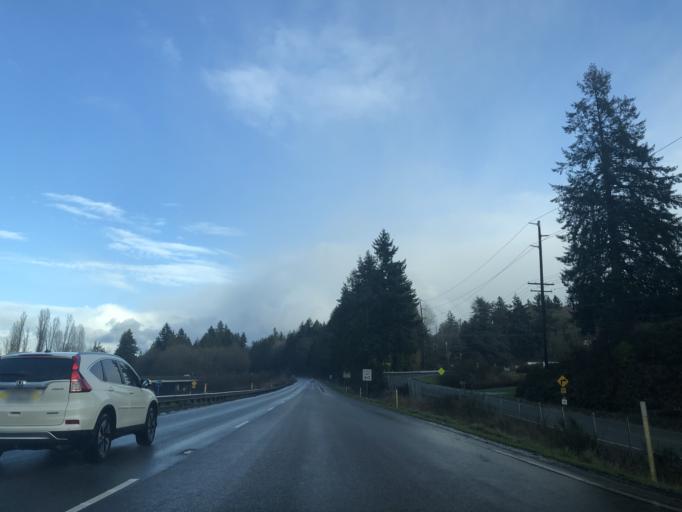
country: US
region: Washington
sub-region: Kitsap County
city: Navy Yard City
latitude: 47.5273
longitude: -122.6813
